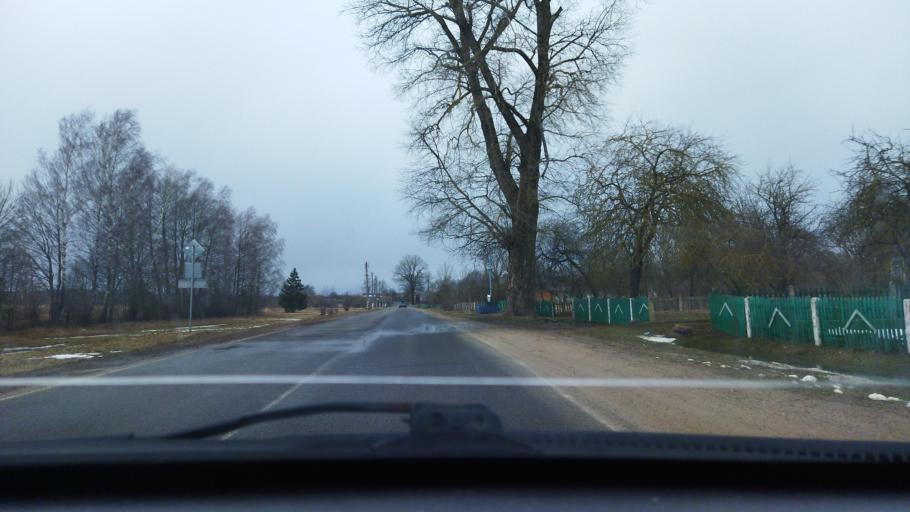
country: BY
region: Minsk
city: Svir
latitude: 54.8732
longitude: 26.3994
